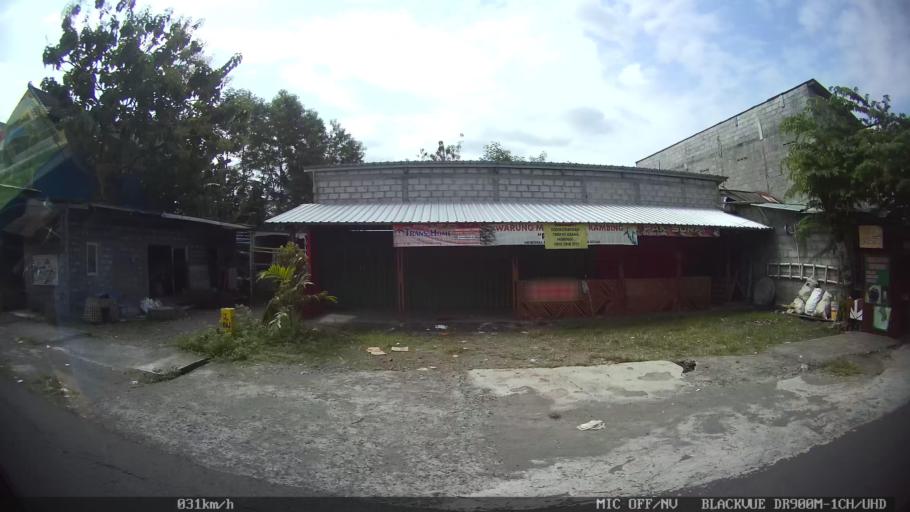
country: ID
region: Daerah Istimewa Yogyakarta
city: Depok
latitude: -7.7599
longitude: 110.4260
